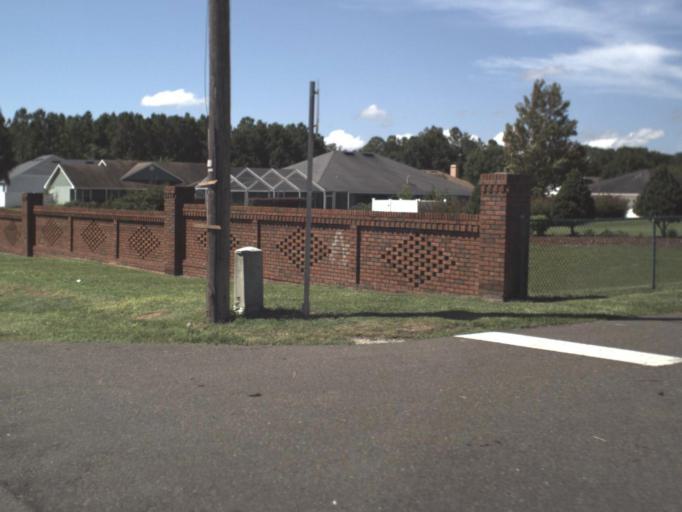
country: US
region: Florida
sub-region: Polk County
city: Auburndale
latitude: 28.1047
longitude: -81.7893
